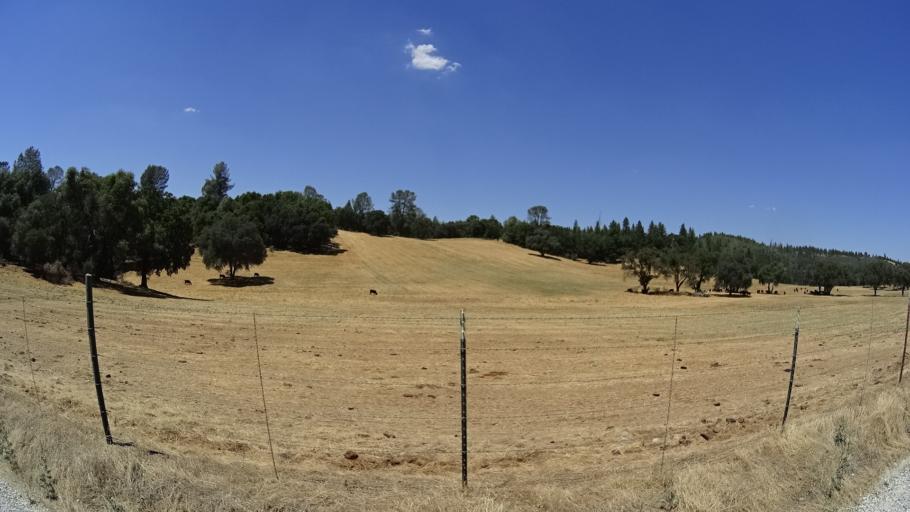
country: US
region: California
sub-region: Calaveras County
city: Murphys
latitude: 38.1110
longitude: -120.4771
